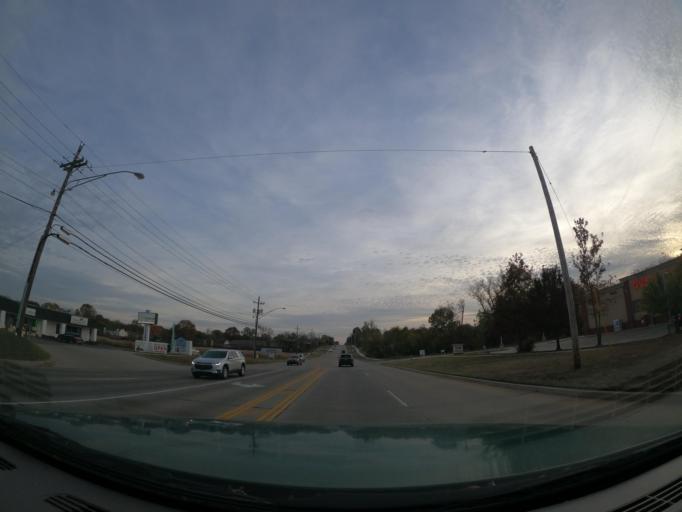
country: US
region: Oklahoma
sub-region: Tulsa County
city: Broken Arrow
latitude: 35.9879
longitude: -95.7974
